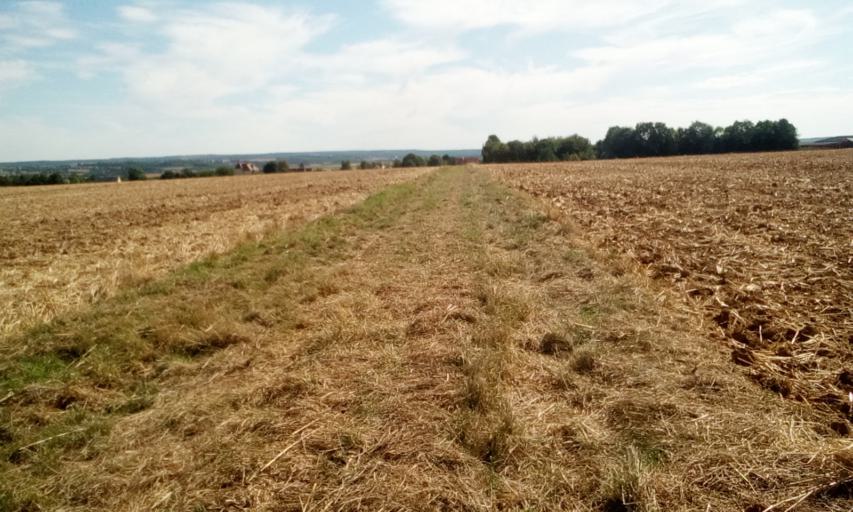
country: FR
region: Lower Normandy
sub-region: Departement du Calvados
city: Bully
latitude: 49.1159
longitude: -0.4320
